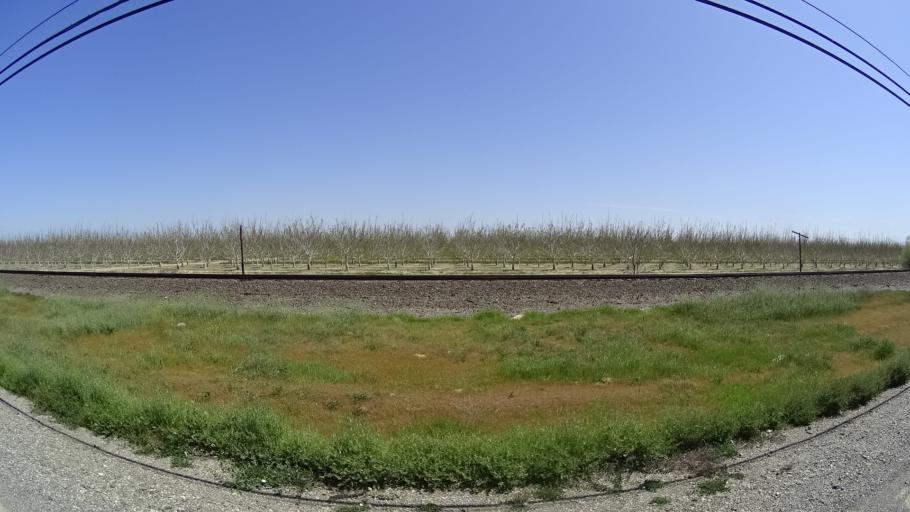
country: US
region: California
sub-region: Glenn County
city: Willows
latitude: 39.6037
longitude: -122.1940
